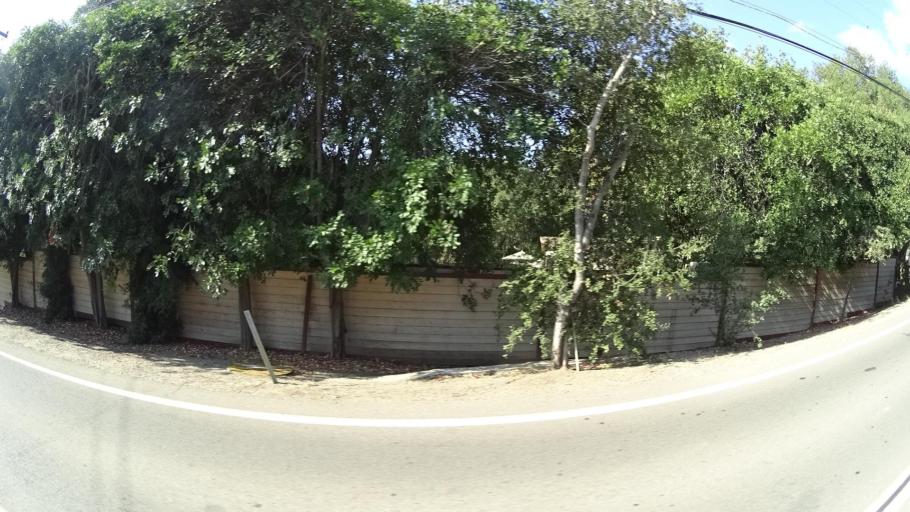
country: US
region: California
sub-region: San Diego County
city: Eucalyptus Hills
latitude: 32.8749
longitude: -116.9521
